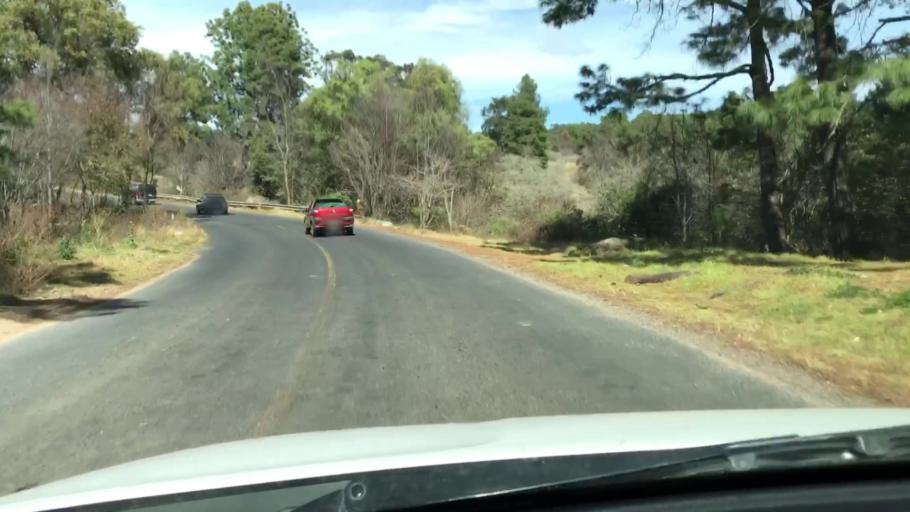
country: MX
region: Jalisco
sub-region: Amacueca
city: Tepec
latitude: 20.0889
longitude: -103.7148
